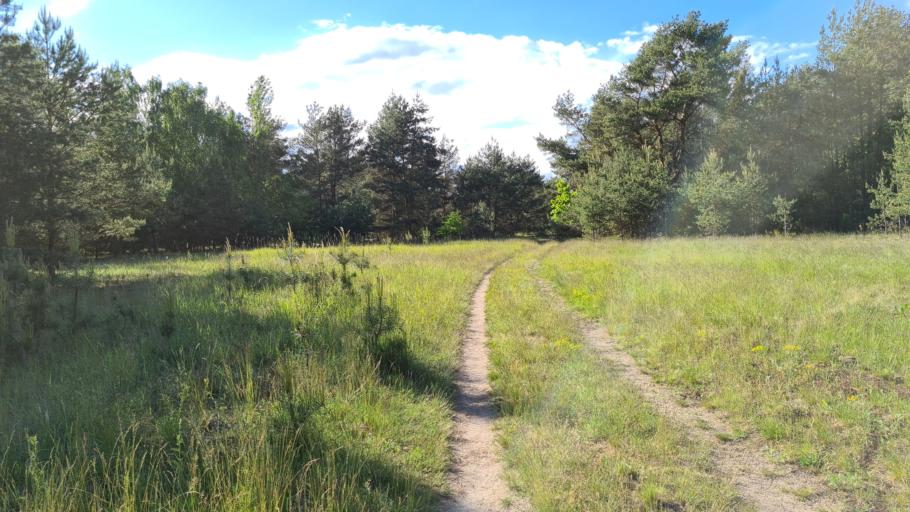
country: DE
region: Brandenburg
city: Eisenhuettenstadt
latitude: 52.1574
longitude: 14.6613
